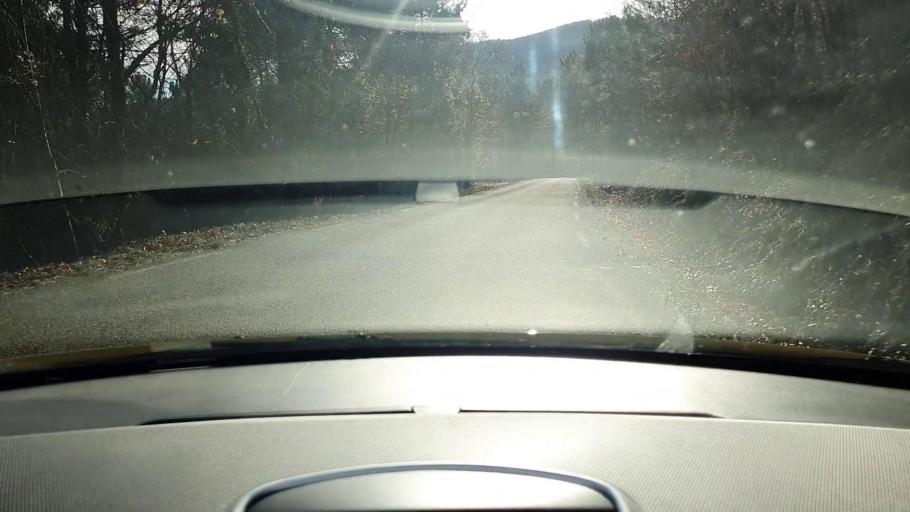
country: FR
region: Languedoc-Roussillon
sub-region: Departement du Gard
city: Branoux-les-Taillades
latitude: 44.2225
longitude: 3.9812
